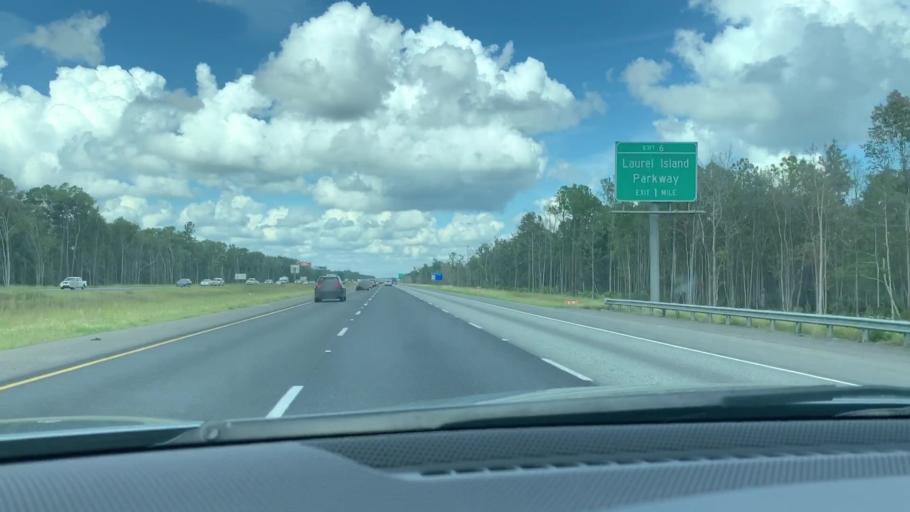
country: US
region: Georgia
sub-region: Camden County
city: Kingsland
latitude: 30.8065
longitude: -81.6622
